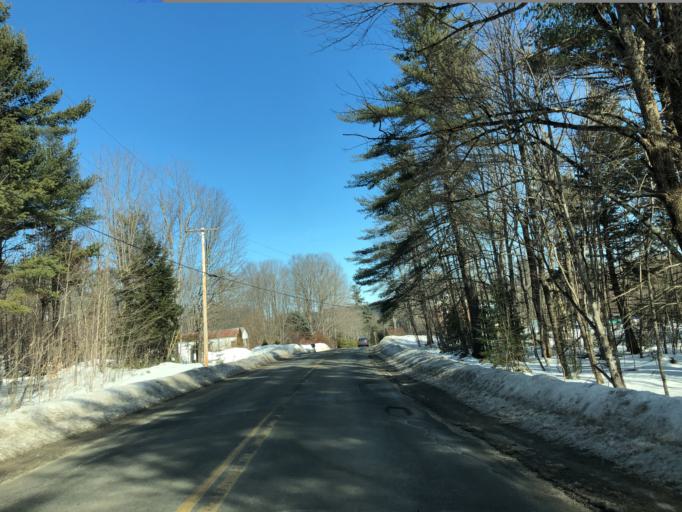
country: US
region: Maine
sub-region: Oxford County
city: Hebron
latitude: 44.1982
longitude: -70.3601
